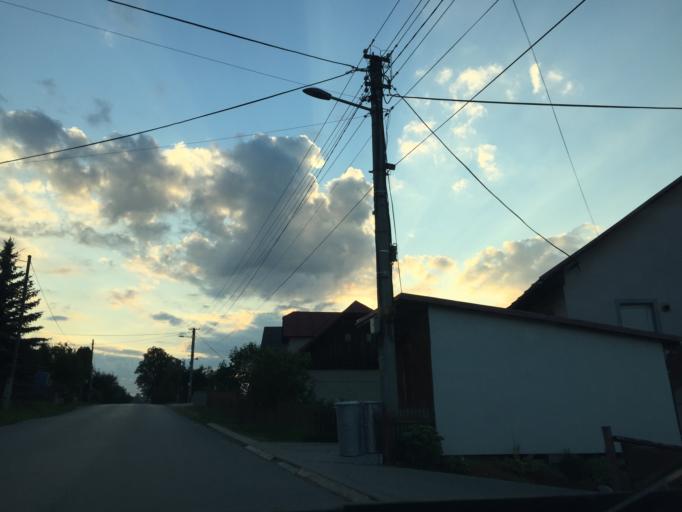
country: PL
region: Silesian Voivodeship
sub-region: Powiat zywiecki
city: Korbielow
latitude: 49.4615
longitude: 19.3499
